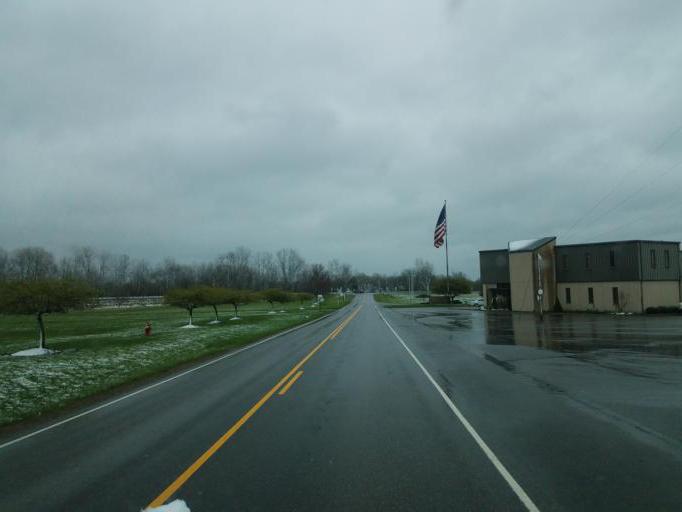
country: US
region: Ohio
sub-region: Knox County
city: Fredericktown
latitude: 40.4928
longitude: -82.5609
